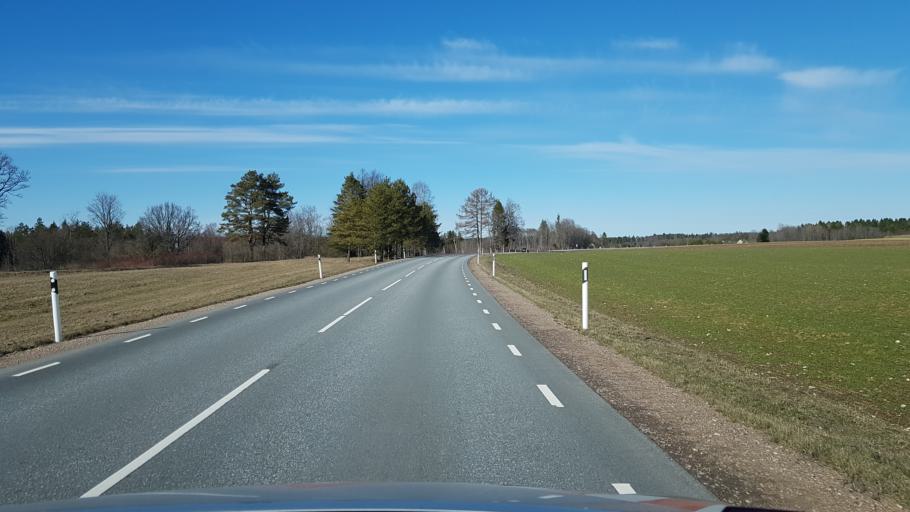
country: EE
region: Laeaene-Virumaa
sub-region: Tapa vald
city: Tapa
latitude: 59.3735
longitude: 26.0021
